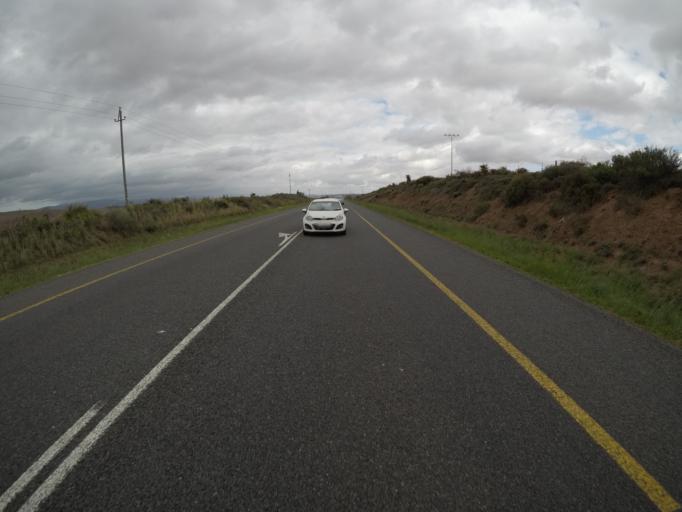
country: ZA
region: Western Cape
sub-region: Eden District Municipality
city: Riversdale
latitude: -34.1145
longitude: 20.8977
